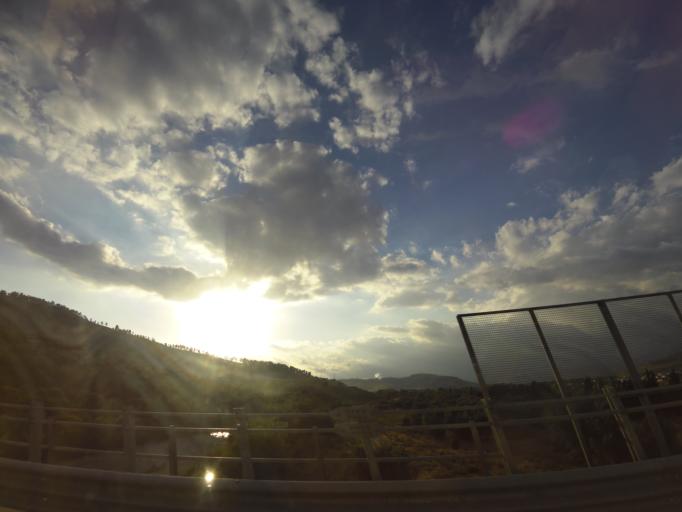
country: IT
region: Calabria
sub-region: Provincia di Catanzaro
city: Catanzaro
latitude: 38.8485
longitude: 16.5739
